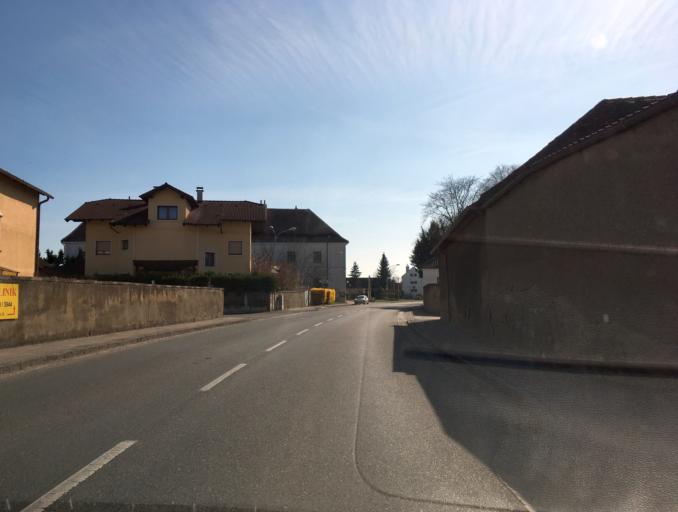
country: AT
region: Lower Austria
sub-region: Politischer Bezirk Wien-Umgebung
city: Schwadorf
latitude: 48.0509
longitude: 16.6069
